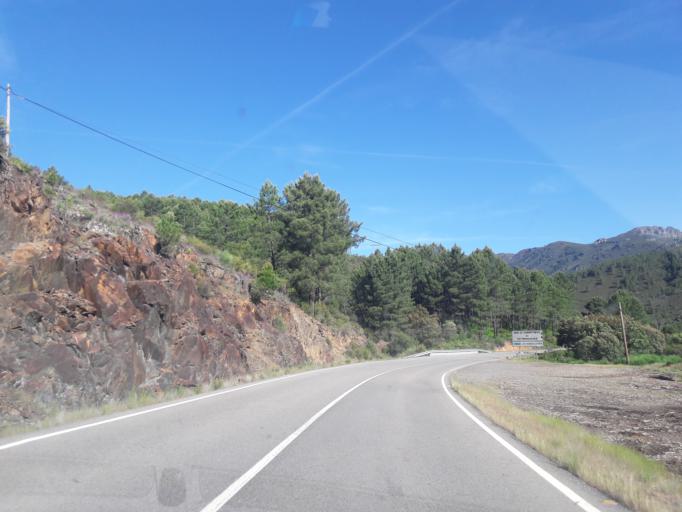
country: ES
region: Castille and Leon
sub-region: Provincia de Salamanca
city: Herguijuela de la Sierra
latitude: 40.4077
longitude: -6.0933
